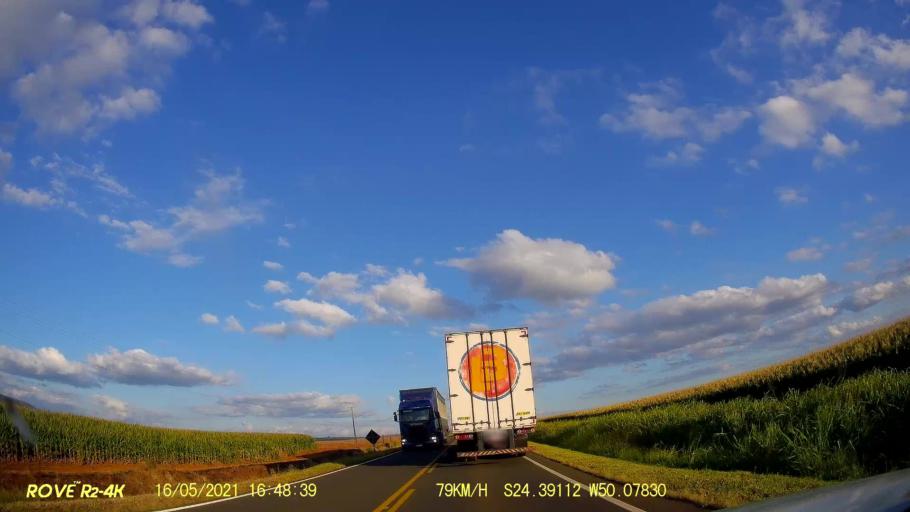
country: BR
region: Parana
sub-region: Pirai Do Sul
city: Pirai do Sul
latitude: -24.3913
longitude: -50.0785
